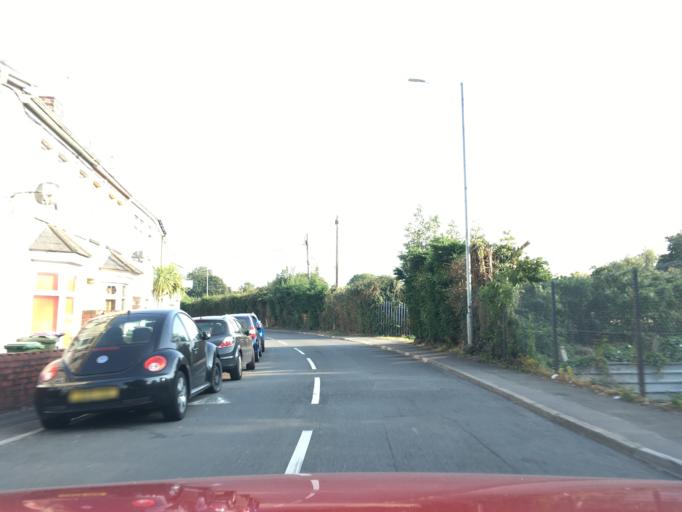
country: GB
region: Wales
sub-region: Torfaen County Borough
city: Cwmbran
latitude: 51.6597
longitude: -3.0147
